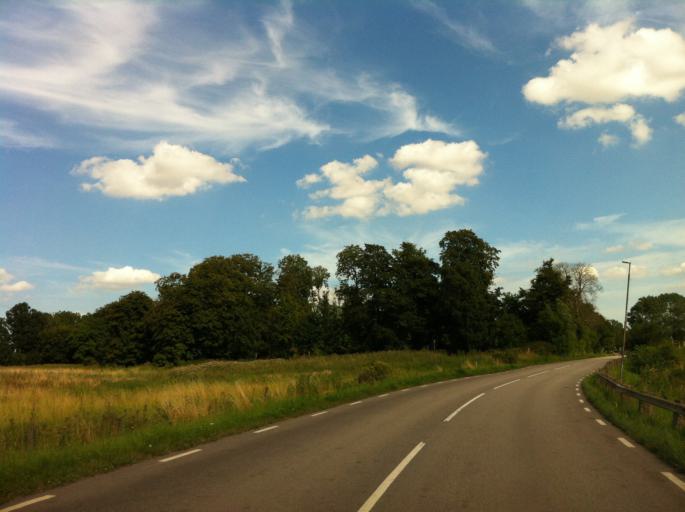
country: SE
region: Skane
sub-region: Landskrona
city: Asmundtorp
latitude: 55.8943
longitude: 12.9629
